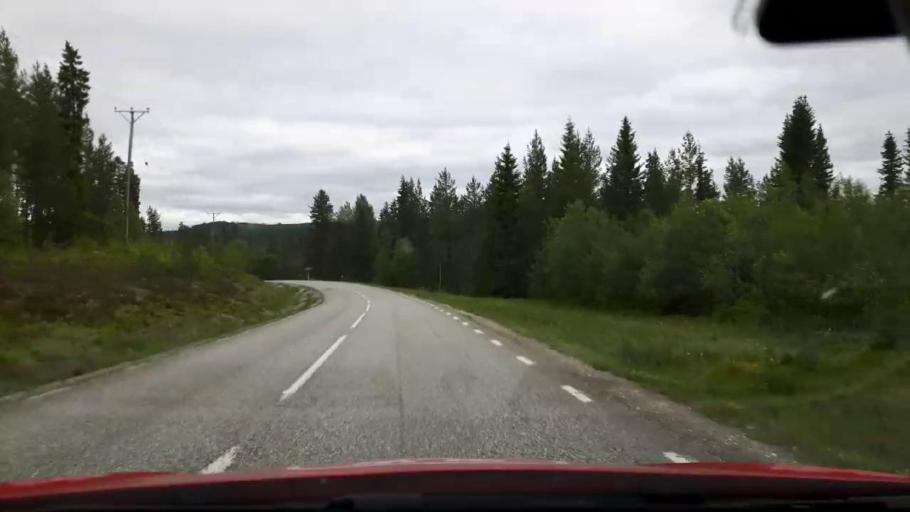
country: SE
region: Jaemtland
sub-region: Stroemsunds Kommun
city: Stroemsund
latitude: 63.2939
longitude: 15.7706
